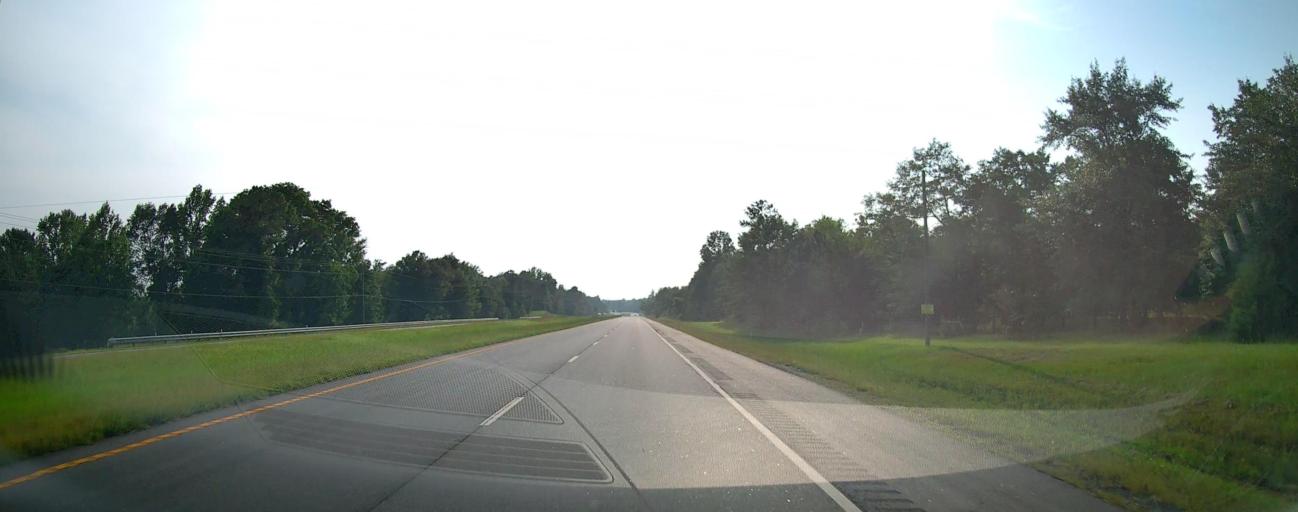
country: US
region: Georgia
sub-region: Talbot County
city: Talbotton
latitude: 32.5752
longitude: -84.5810
